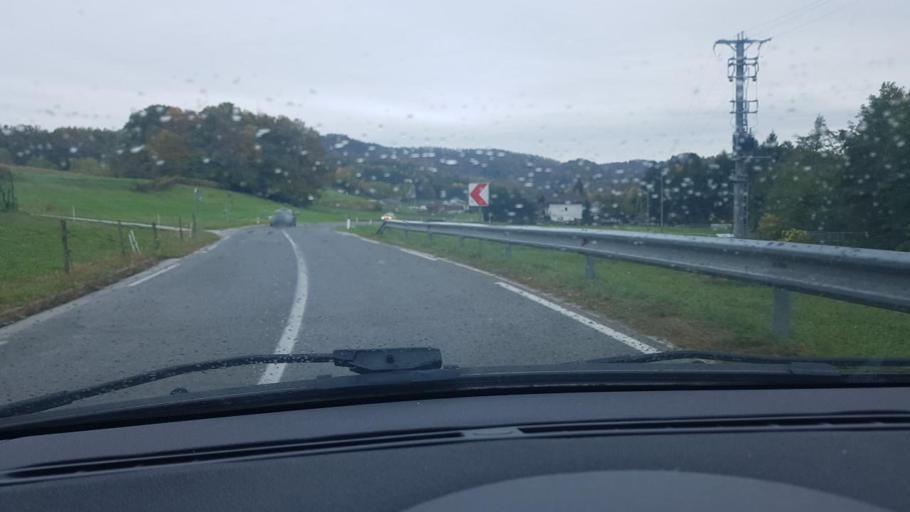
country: SI
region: Rogatec
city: Rogatec
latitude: 46.2467
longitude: 15.7000
